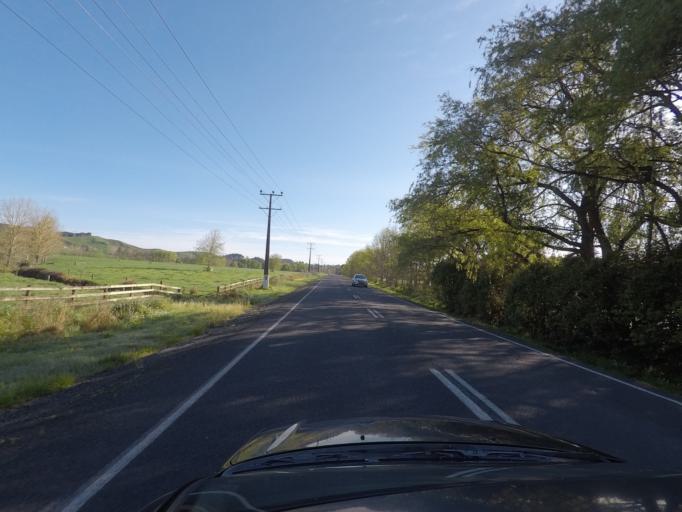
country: NZ
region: Auckland
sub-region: Auckland
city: Red Hill
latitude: -37.0098
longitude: 174.9517
